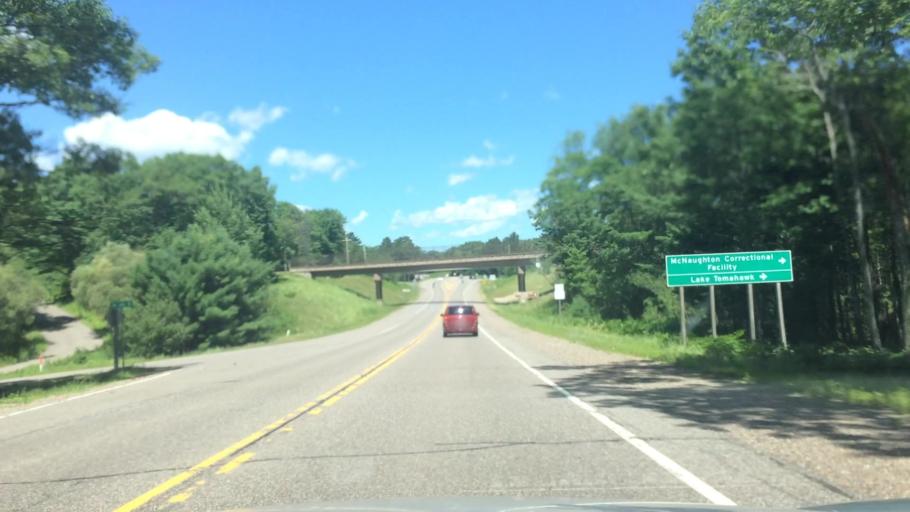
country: US
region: Wisconsin
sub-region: Vilas County
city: Lac du Flambeau
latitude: 45.7826
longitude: -89.7130
